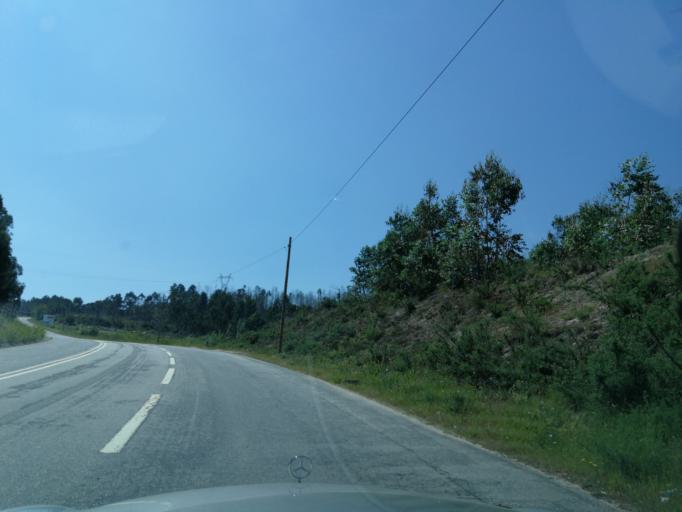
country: PT
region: Braga
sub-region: Braga
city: Adaufe
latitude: 41.5614
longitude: -8.3578
